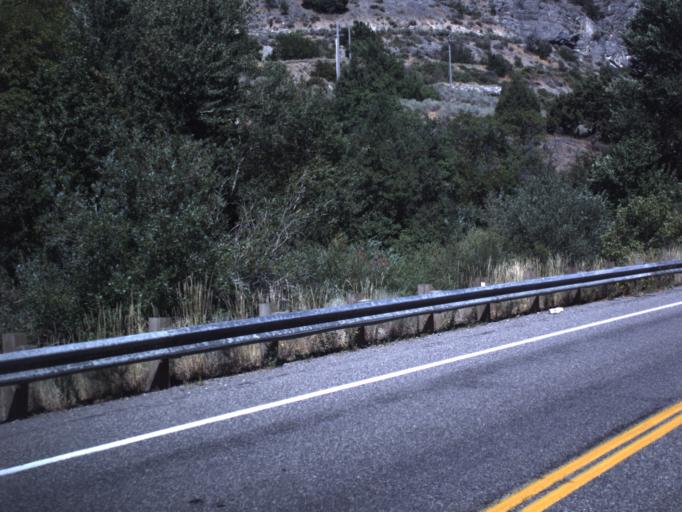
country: US
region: Utah
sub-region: Cache County
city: North Logan
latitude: 41.7423
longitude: -111.7788
